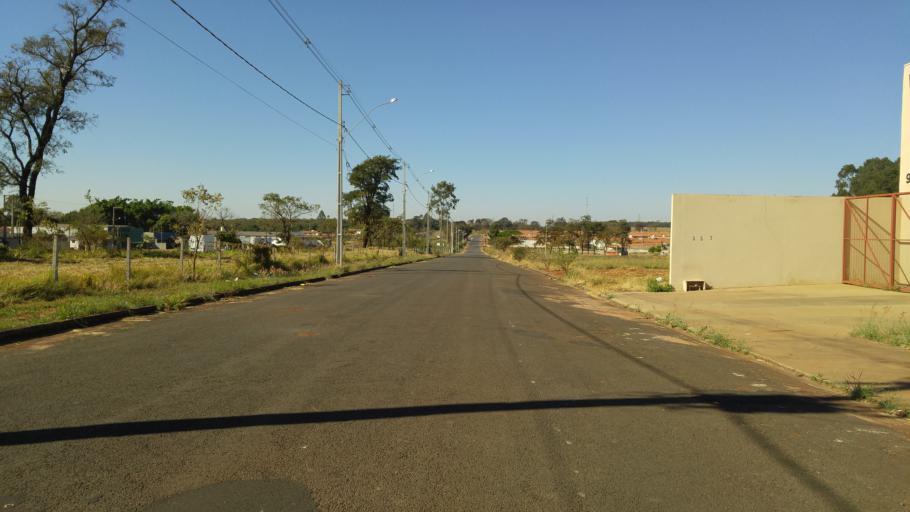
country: BR
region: Sao Paulo
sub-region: Paraguacu Paulista
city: Paraguacu Paulista
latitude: -22.4395
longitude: -50.5858
